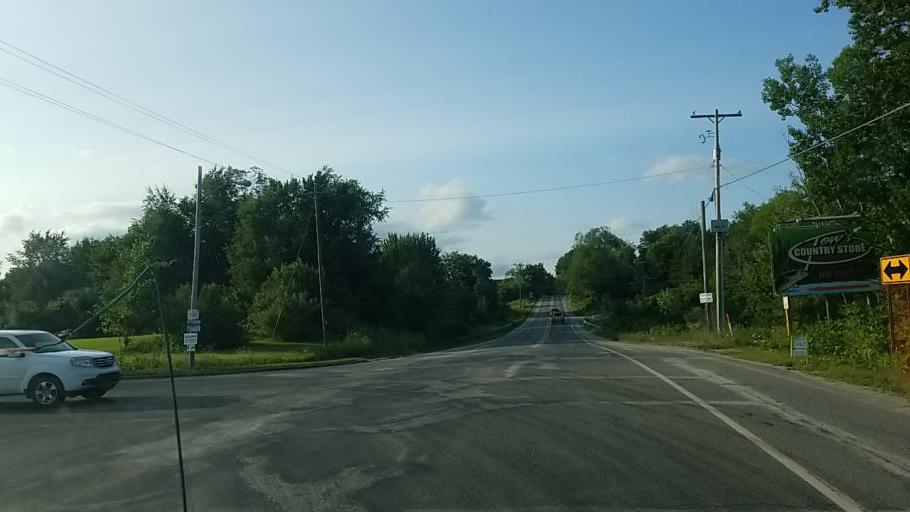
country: US
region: Michigan
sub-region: Montcalm County
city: Greenville
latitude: 43.2337
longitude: -85.3520
